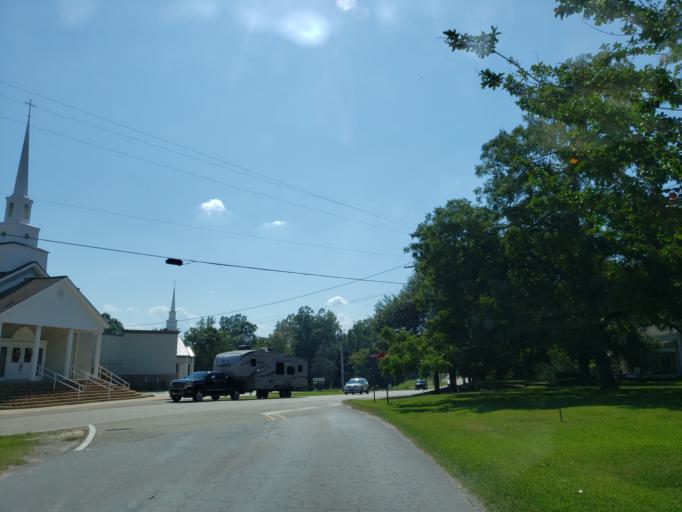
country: US
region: Mississippi
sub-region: Covington County
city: Collins
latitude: 31.5624
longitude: -89.5011
